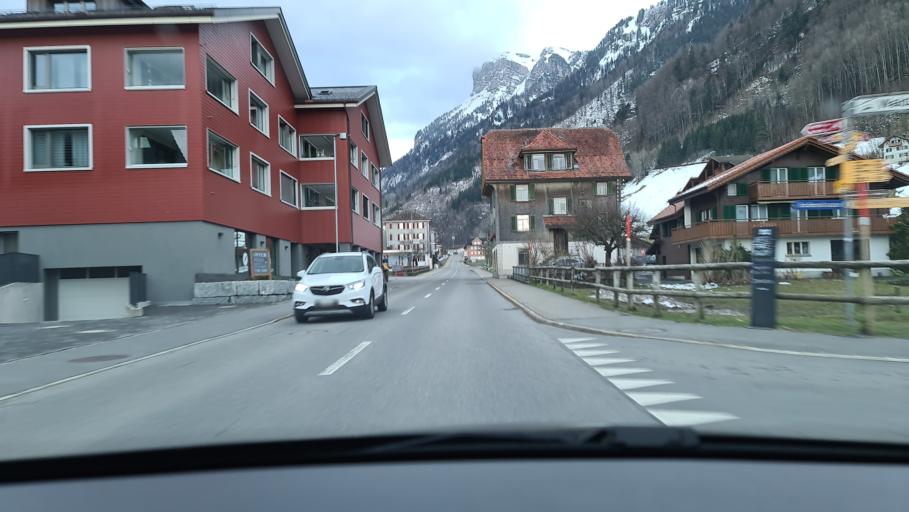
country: CH
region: Nidwalden
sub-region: Nidwalden
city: Emmetten
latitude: 46.9568
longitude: 8.5133
